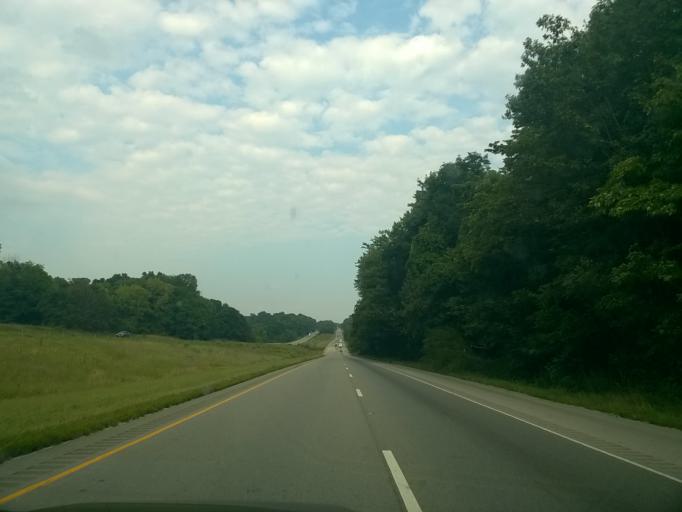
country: US
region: Indiana
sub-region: Putnam County
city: Cloverdale
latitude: 39.5119
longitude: -86.9283
